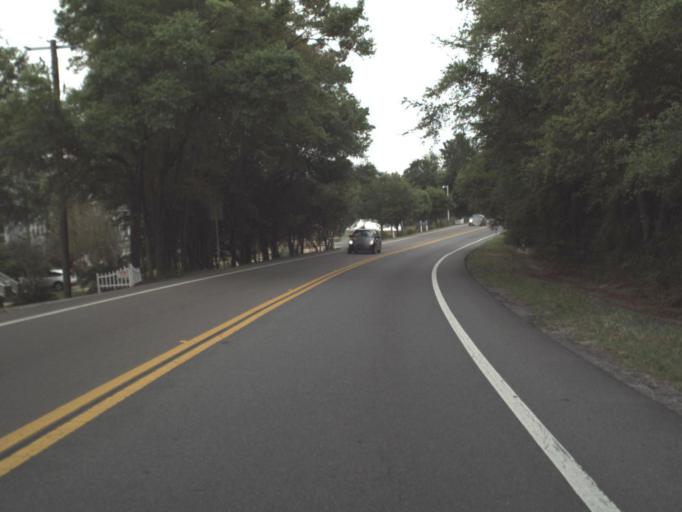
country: US
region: Florida
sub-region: Escambia County
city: Ferry Pass
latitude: 30.5171
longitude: -87.1665
